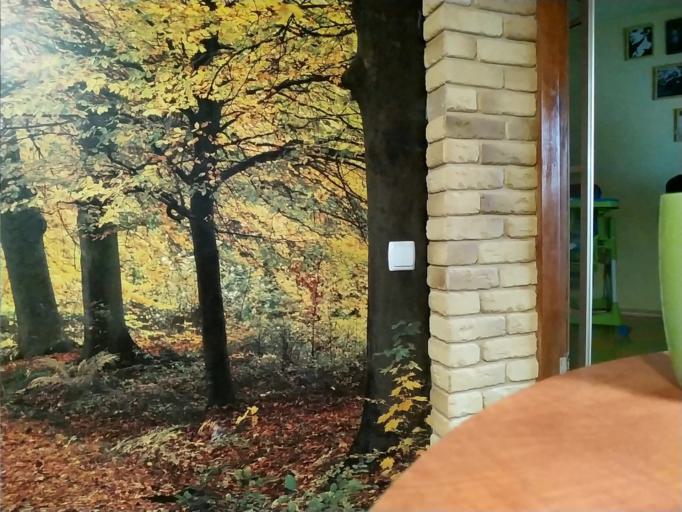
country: RU
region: Tverskaya
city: Staraya Toropa
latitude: 56.3517
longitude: 31.8110
